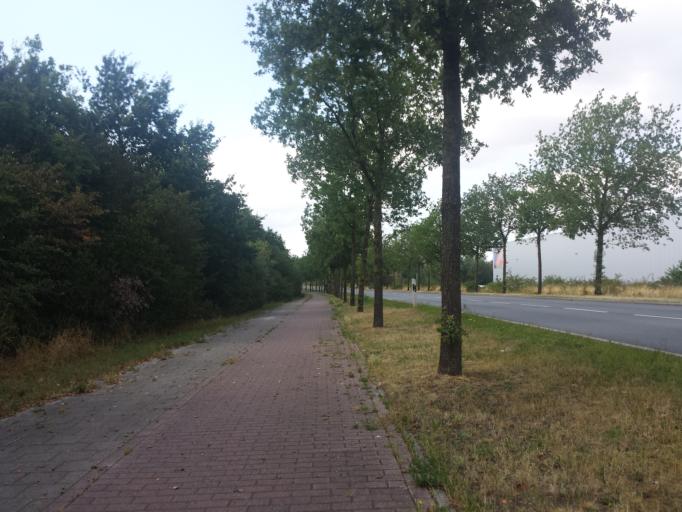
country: DE
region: Lower Saxony
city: Stuhr
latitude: 53.0833
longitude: 8.7331
